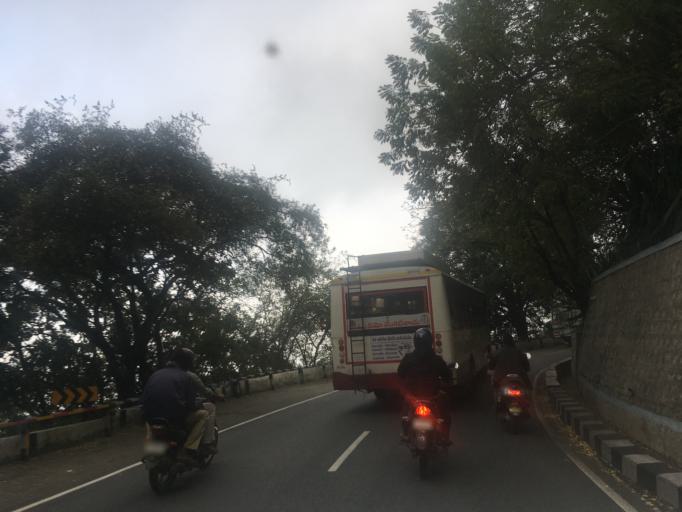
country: IN
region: Andhra Pradesh
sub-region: Chittoor
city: Tirumala
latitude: 13.6673
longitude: 79.3482
